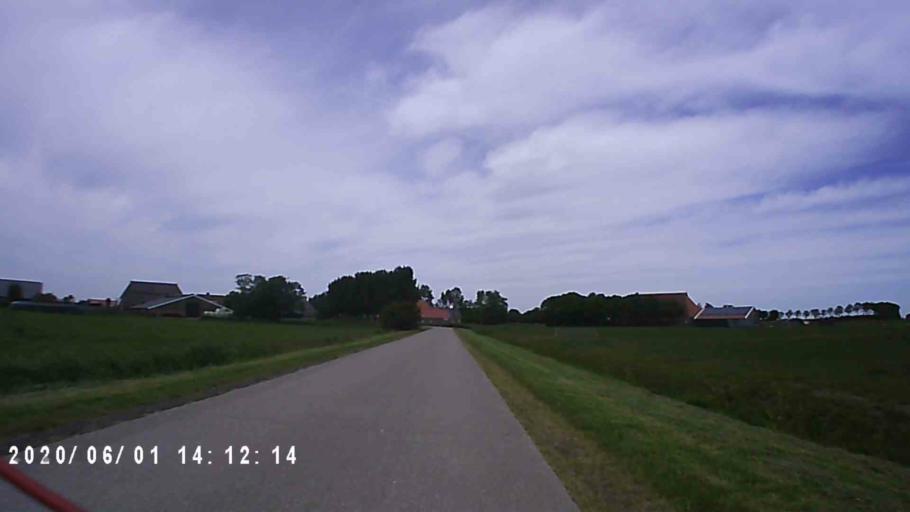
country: NL
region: Friesland
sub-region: Gemeente Littenseradiel
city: Winsum
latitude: 53.1294
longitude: 5.6502
